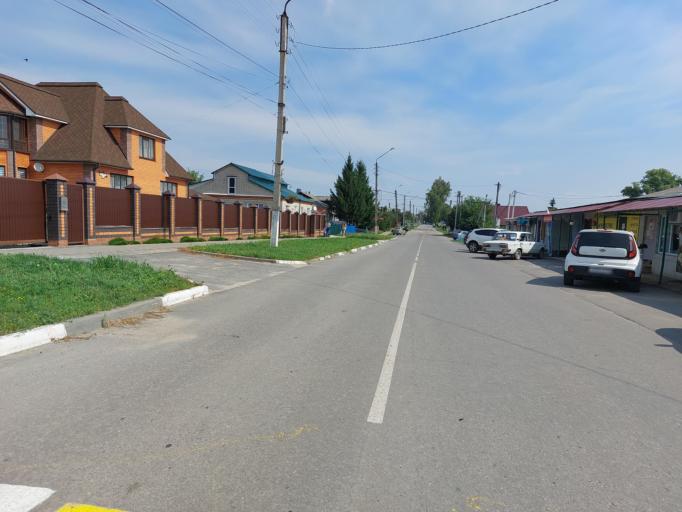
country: RU
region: Lipetsk
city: Dolgorukovo
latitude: 52.3231
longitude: 38.3569
